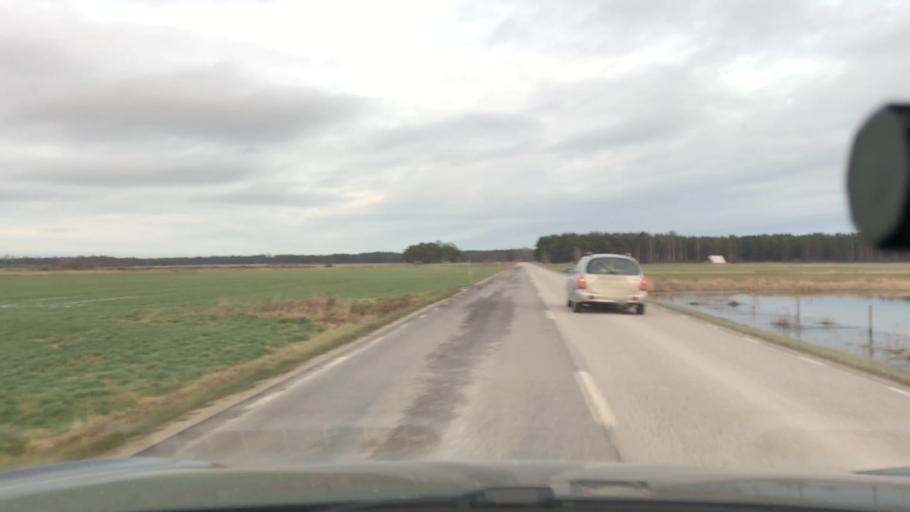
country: SE
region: Gotland
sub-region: Gotland
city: Slite
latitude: 57.7135
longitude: 18.5465
